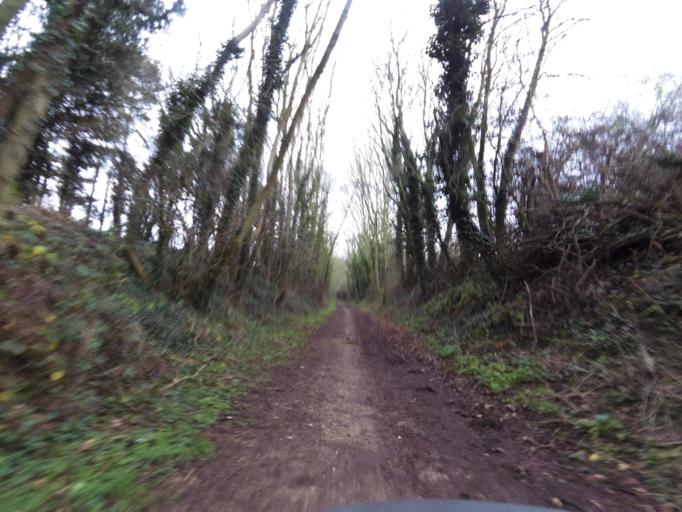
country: GB
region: England
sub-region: Norfolk
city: Mattishall
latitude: 52.7378
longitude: 1.0958
